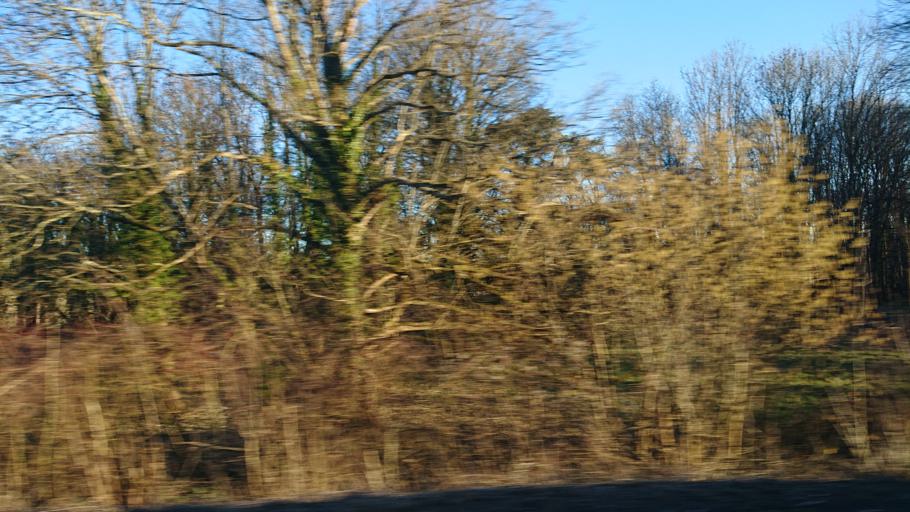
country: FR
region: Auvergne
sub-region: Departement du Puy-de-Dome
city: Randan
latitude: 46.0138
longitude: 3.3670
